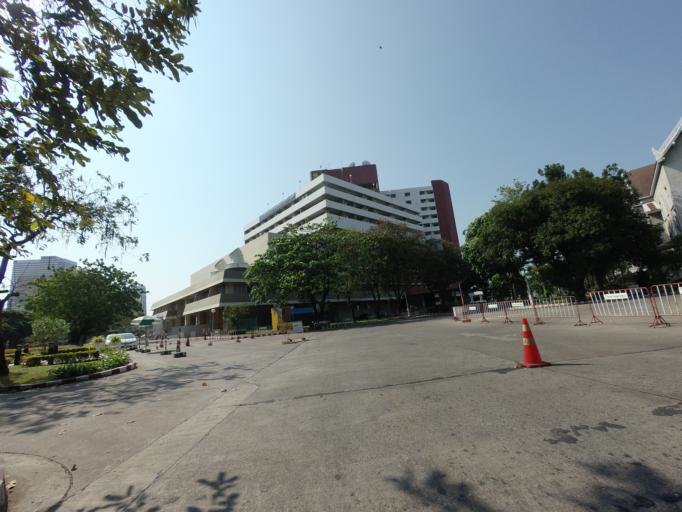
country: TH
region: Bangkok
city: Khlong Toei
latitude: 13.7240
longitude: 100.5547
